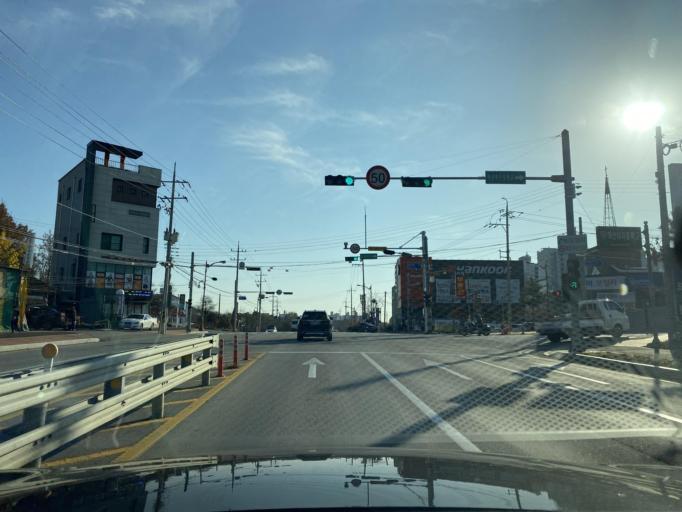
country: KR
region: Chungcheongnam-do
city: Yesan
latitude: 36.6984
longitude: 126.8376
